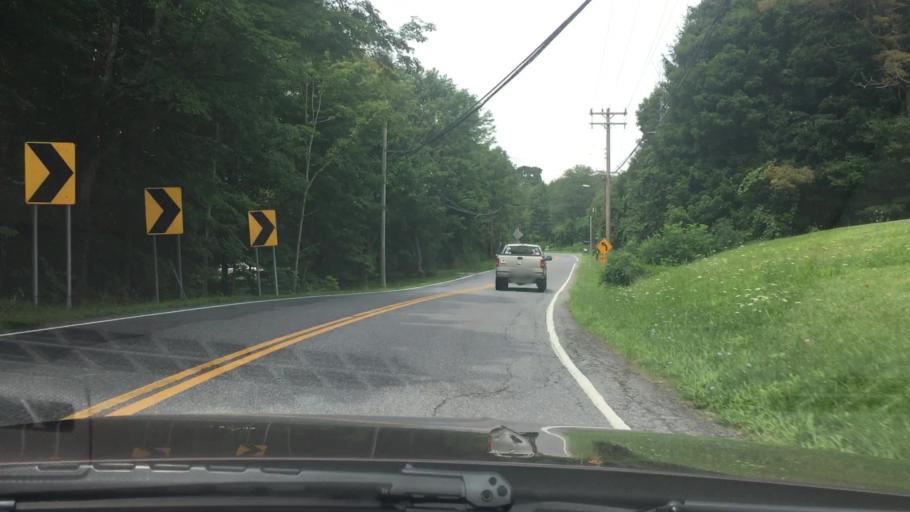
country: US
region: New York
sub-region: Dutchess County
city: Red Oaks Mill
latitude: 41.6525
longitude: -73.8369
